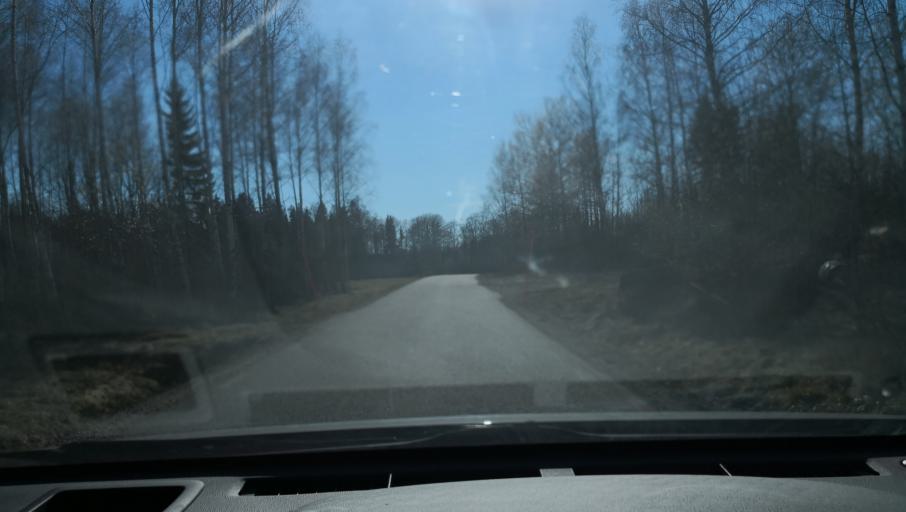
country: SE
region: Dalarna
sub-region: Avesta Kommun
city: Horndal
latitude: 60.0753
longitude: 16.3850
